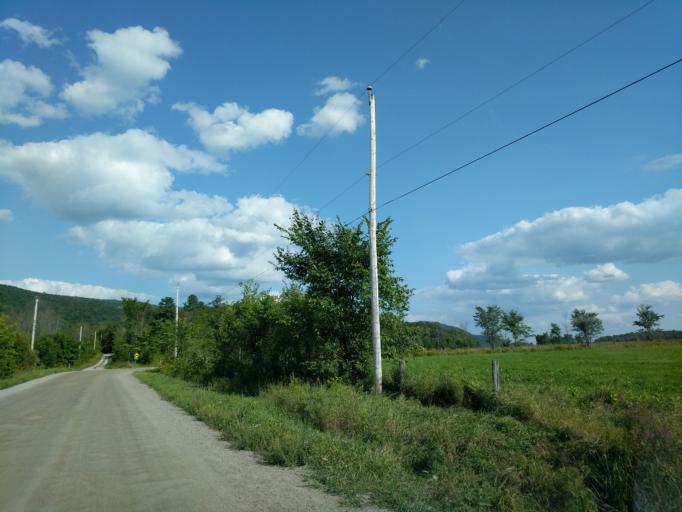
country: CA
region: Quebec
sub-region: Outaouais
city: Wakefield
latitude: 45.5177
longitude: -75.9564
